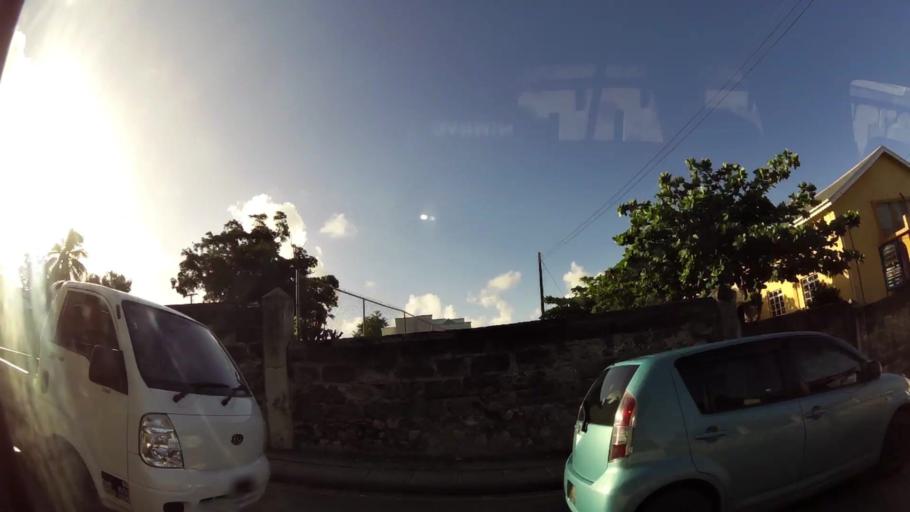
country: BB
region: Saint Michael
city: Bridgetown
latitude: 13.0874
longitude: -59.5990
